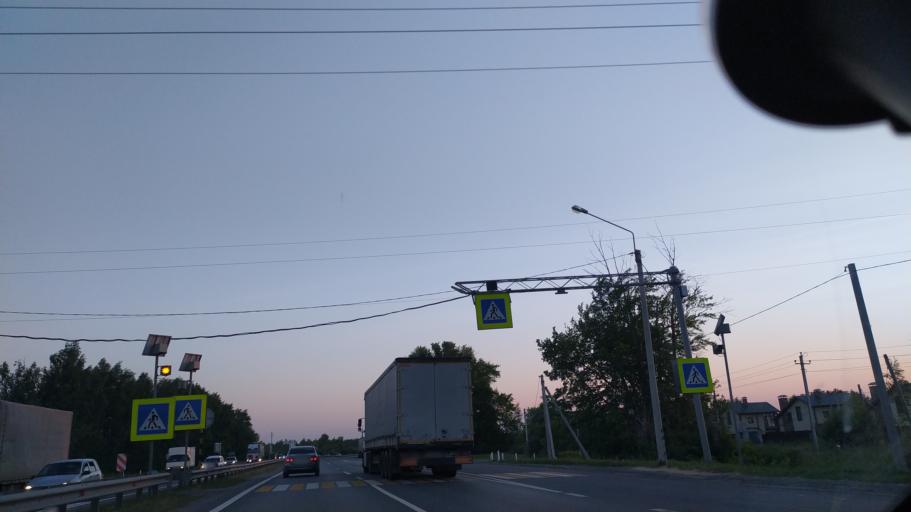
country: RU
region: Chuvashia
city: Ishley
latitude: 56.1018
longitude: 47.0347
